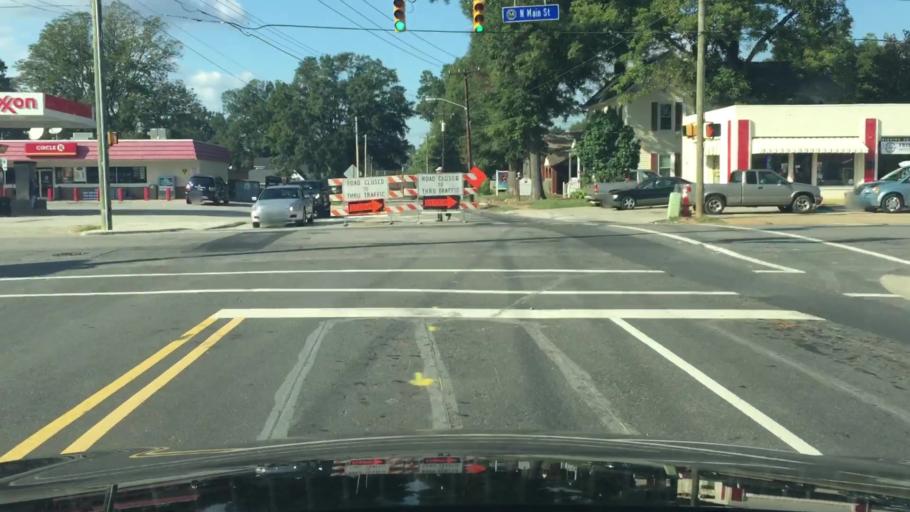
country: US
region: North Carolina
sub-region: Iredell County
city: Mooresville
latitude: 35.5863
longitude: -80.8040
